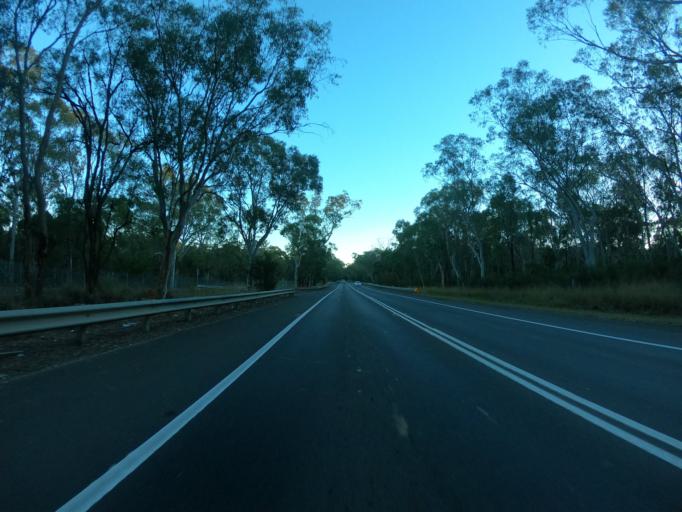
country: AU
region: New South Wales
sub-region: Hawkesbury
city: South Windsor
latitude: -33.6520
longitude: 150.7928
